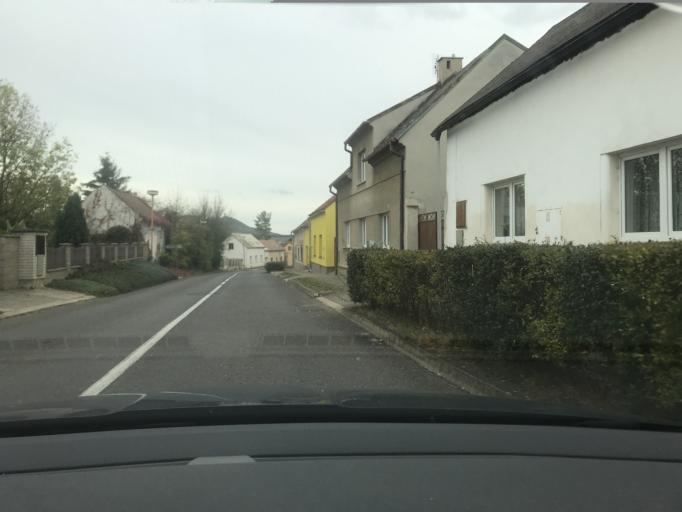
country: CZ
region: Ustecky
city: Trebenice
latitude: 50.4739
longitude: 13.9974
